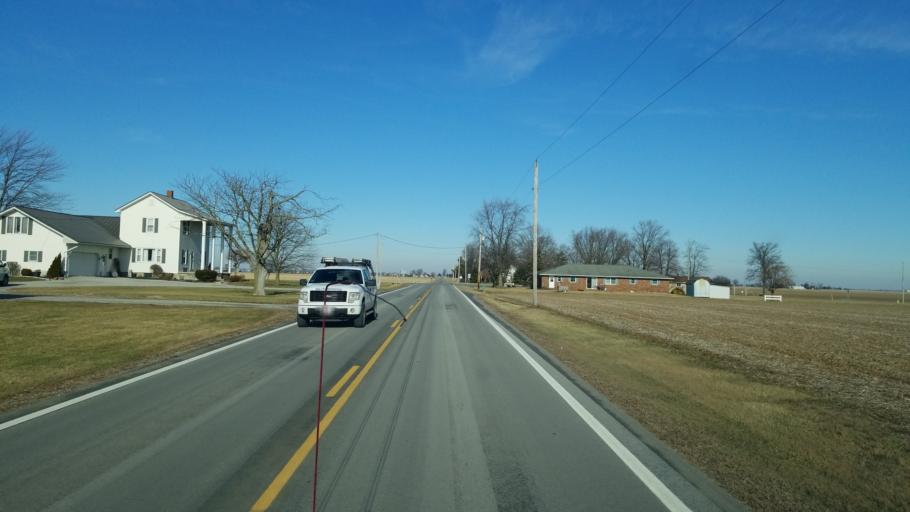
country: US
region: Ohio
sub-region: Putnam County
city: Leipsic
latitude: 41.1220
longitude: -83.9770
